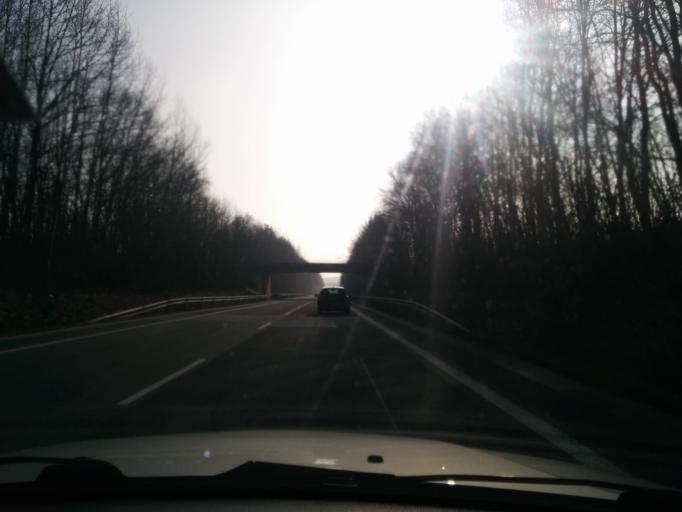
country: DE
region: North Rhine-Westphalia
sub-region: Regierungsbezirk Detmold
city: Blomberg
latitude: 51.9253
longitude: 9.0862
